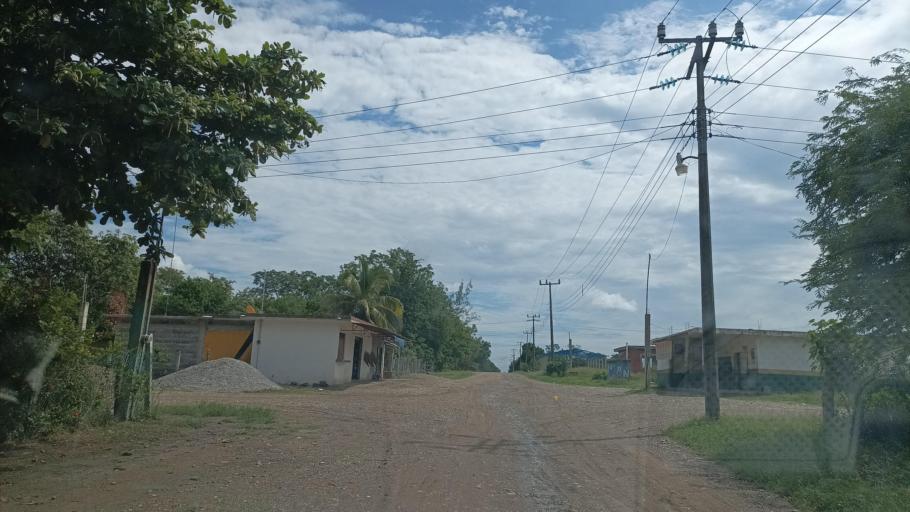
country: MX
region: Veracruz
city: Panuco
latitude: 21.9497
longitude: -98.1368
